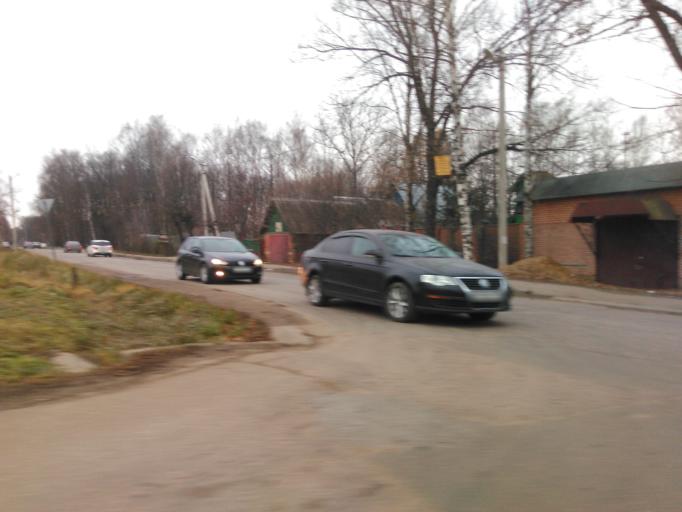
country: RU
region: Moskovskaya
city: Ashukino
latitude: 56.1645
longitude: 37.9474
